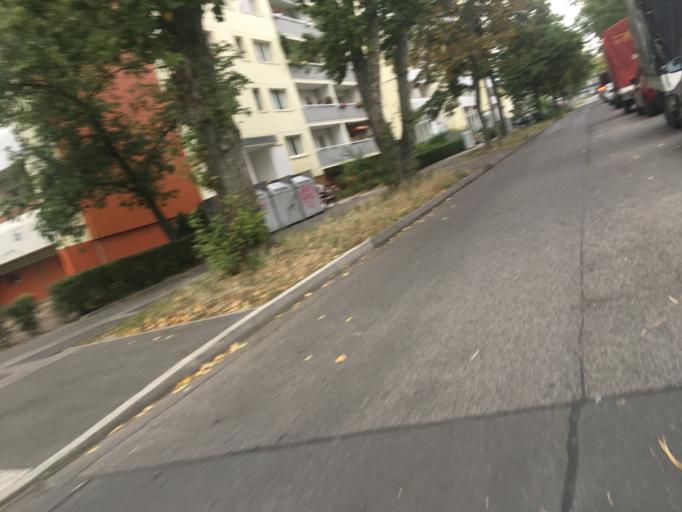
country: DE
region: Berlin
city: Fennpfuhl
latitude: 52.5354
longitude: 13.4806
